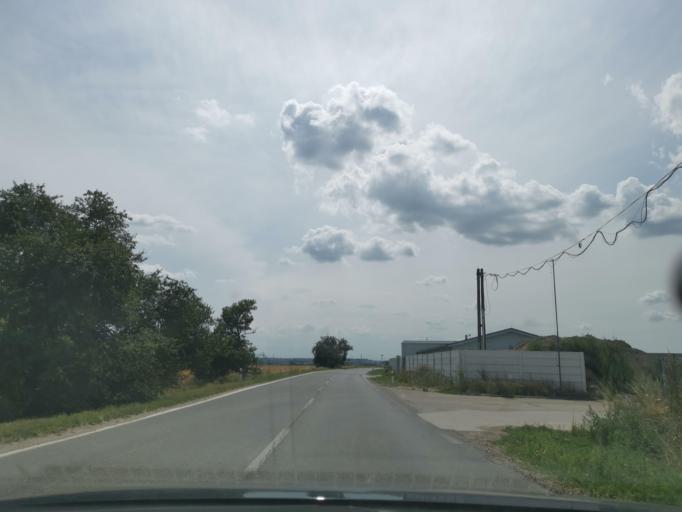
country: SK
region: Bratislavsky
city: Stupava
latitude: 48.2606
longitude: 17.0198
